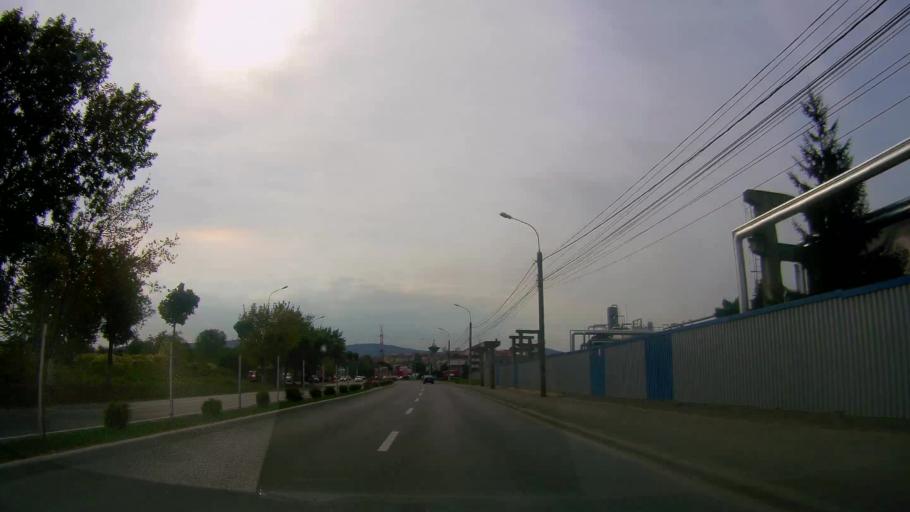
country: RO
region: Salaj
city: Zalau
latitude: 47.2077
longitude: 23.0454
